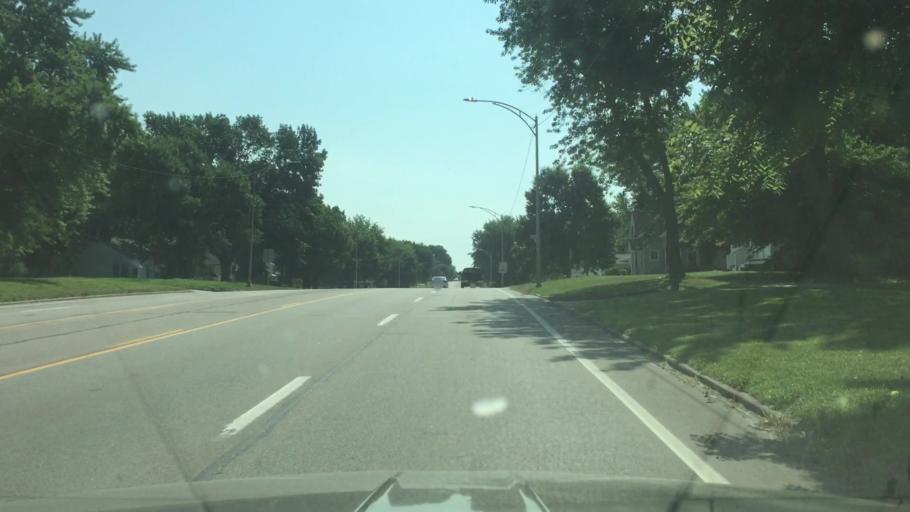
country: US
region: Missouri
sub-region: Pettis County
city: Sedalia
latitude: 38.7032
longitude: -93.2035
